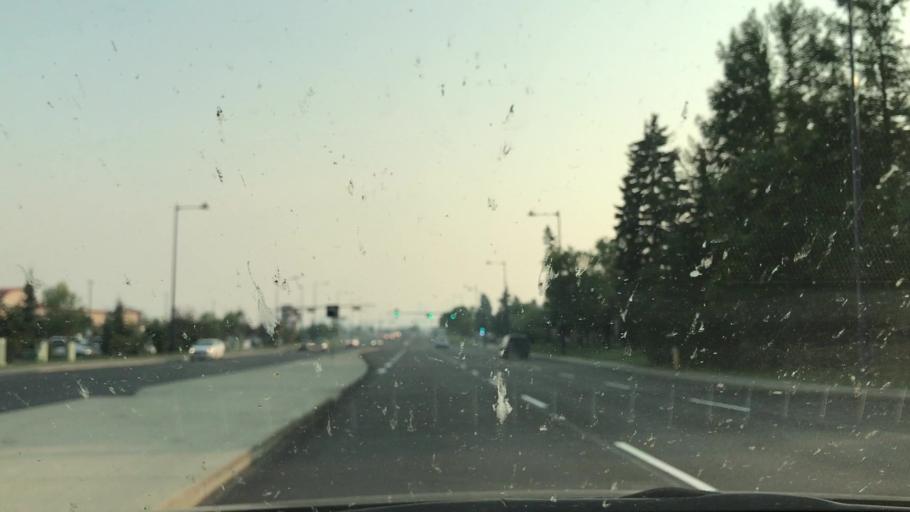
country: CA
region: Alberta
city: Edmonton
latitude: 53.5914
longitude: -113.4319
